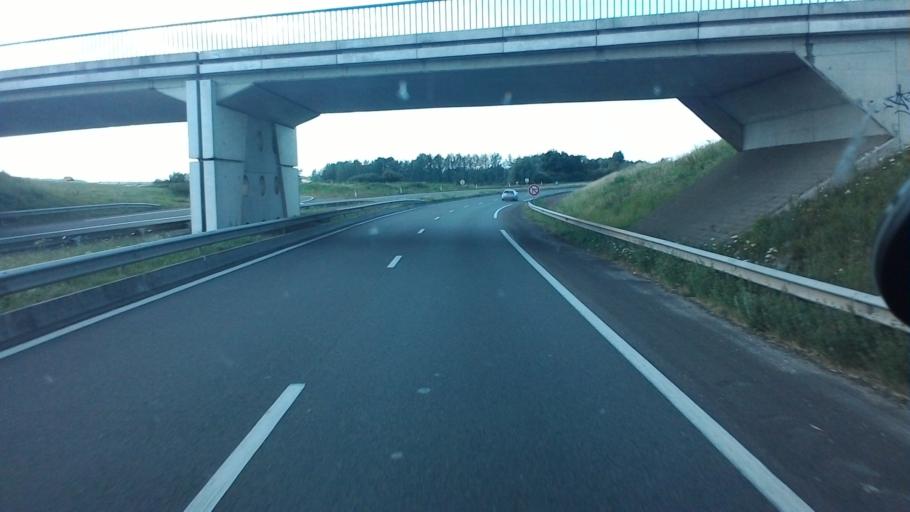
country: FR
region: Franche-Comte
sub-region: Departement de la Haute-Saone
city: Pusey
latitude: 47.6346
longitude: 6.1361
